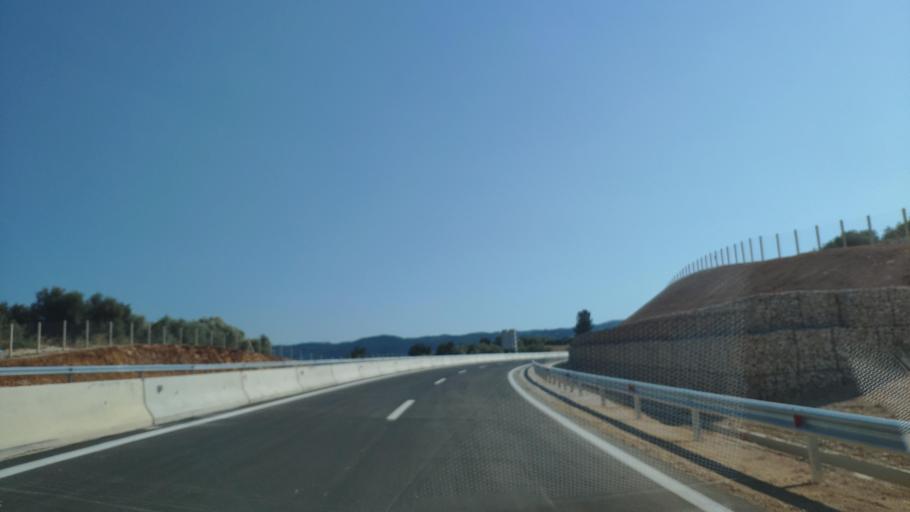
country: GR
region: West Greece
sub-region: Nomos Aitolias kai Akarnanias
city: Stanos
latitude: 38.7748
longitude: 21.1811
